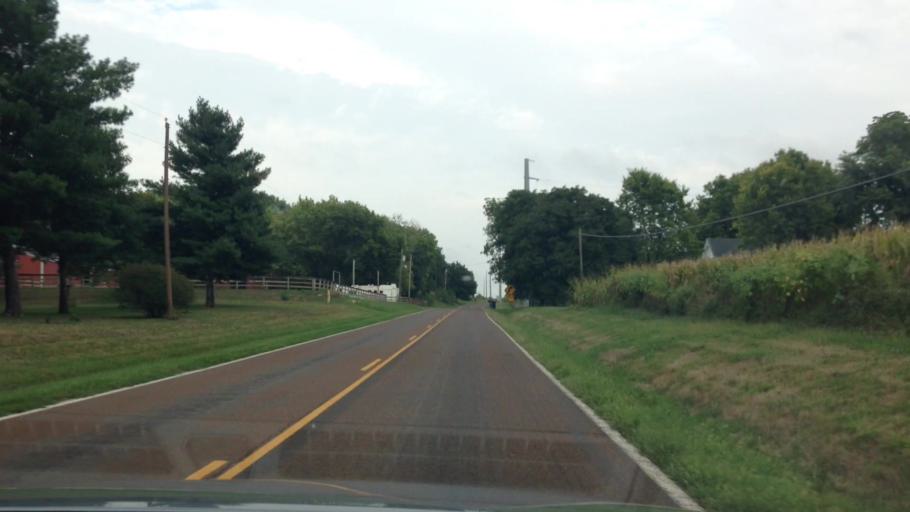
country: US
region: Missouri
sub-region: Clay County
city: Smithville
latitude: 39.4050
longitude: -94.5955
